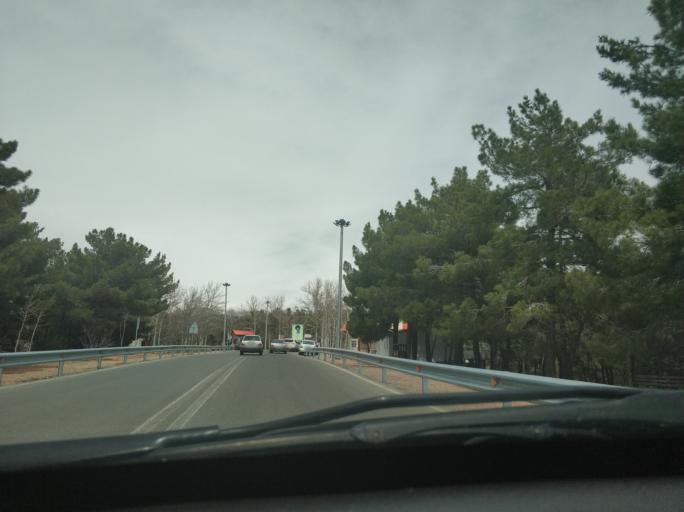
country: IR
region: Tehran
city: Tajrish
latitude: 35.7756
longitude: 51.5528
